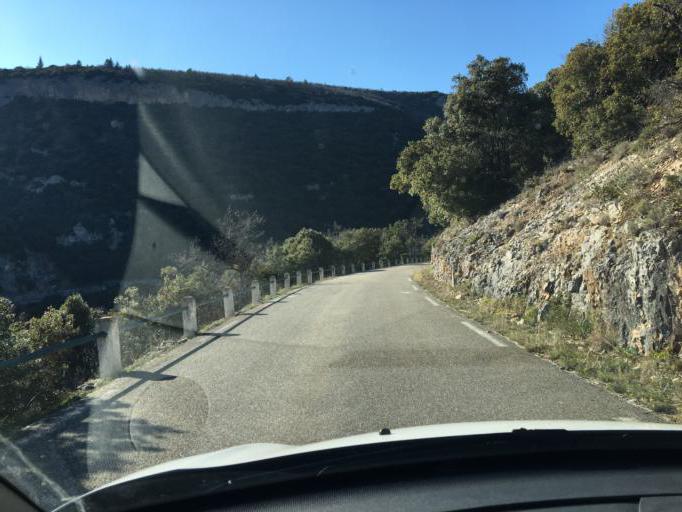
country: FR
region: Provence-Alpes-Cote d'Azur
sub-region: Departement du Vaucluse
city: Villes-sur-Auzon
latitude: 44.0664
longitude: 5.3084
